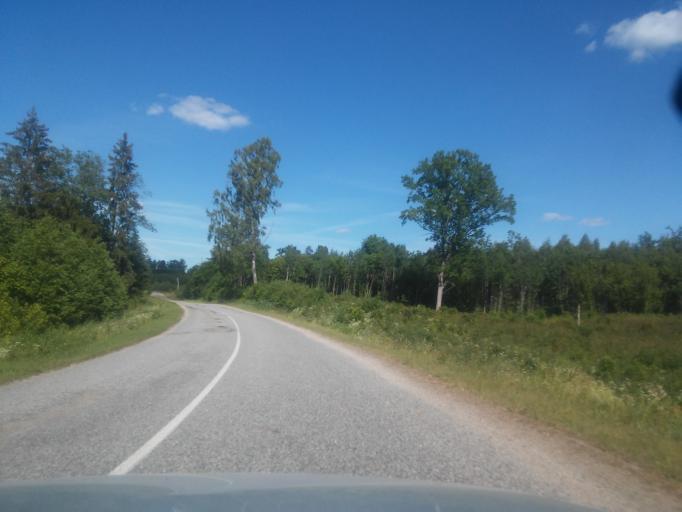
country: LV
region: Skrunda
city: Skrunda
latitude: 56.6090
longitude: 21.9397
